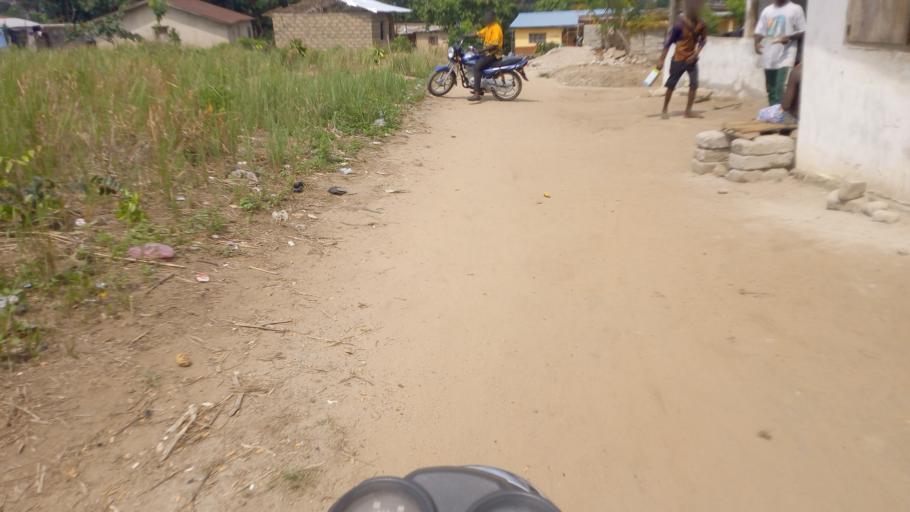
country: SL
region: Western Area
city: Waterloo
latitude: 8.3110
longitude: -13.0621
